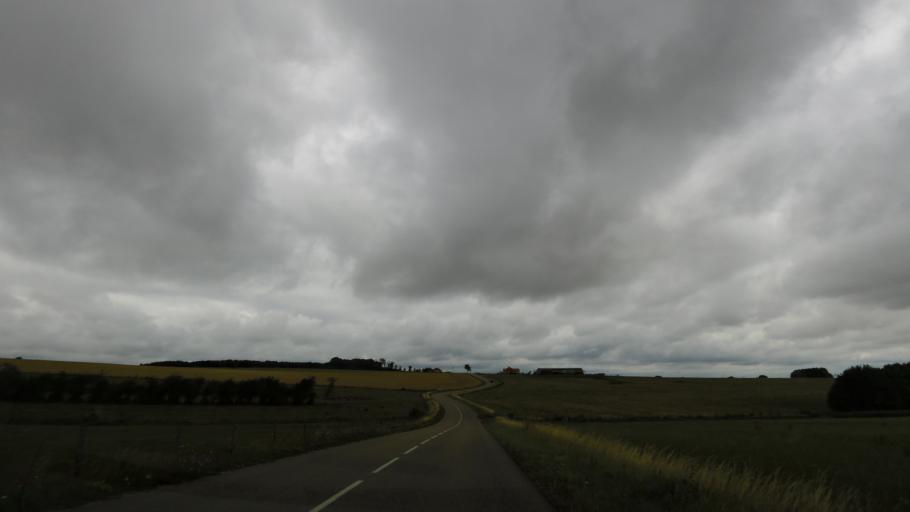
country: FR
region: Lorraine
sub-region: Departement de la Moselle
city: Lorquin
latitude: 48.6380
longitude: 6.9497
